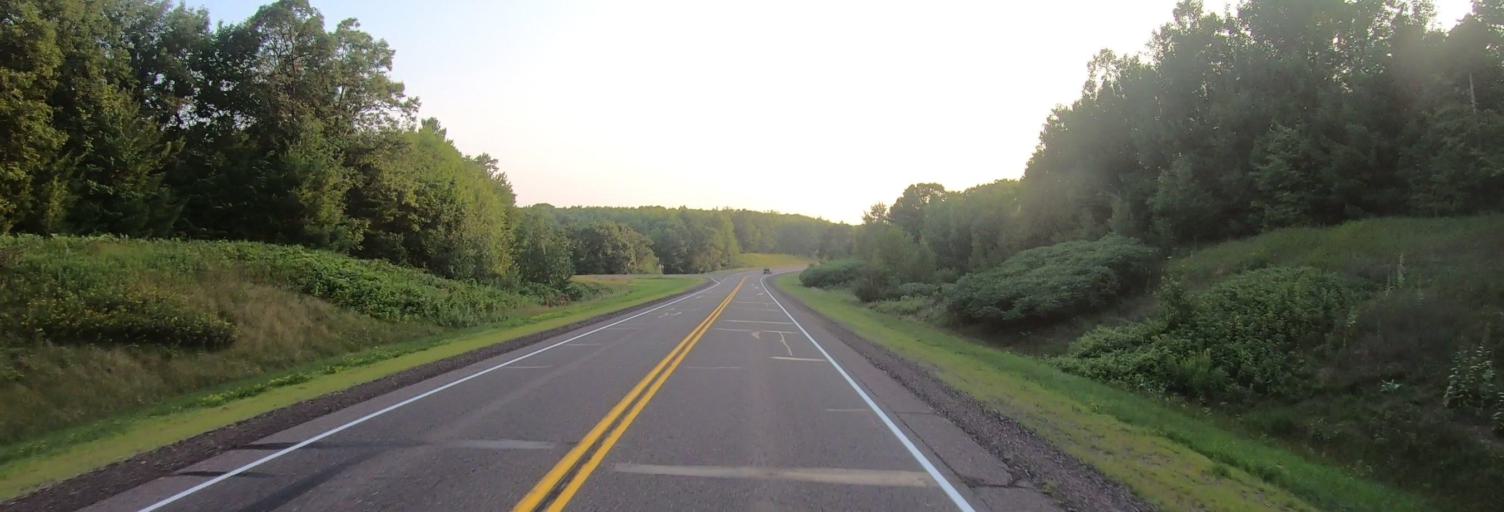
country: US
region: Wisconsin
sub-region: Burnett County
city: Siren
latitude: 45.7669
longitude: -92.4668
